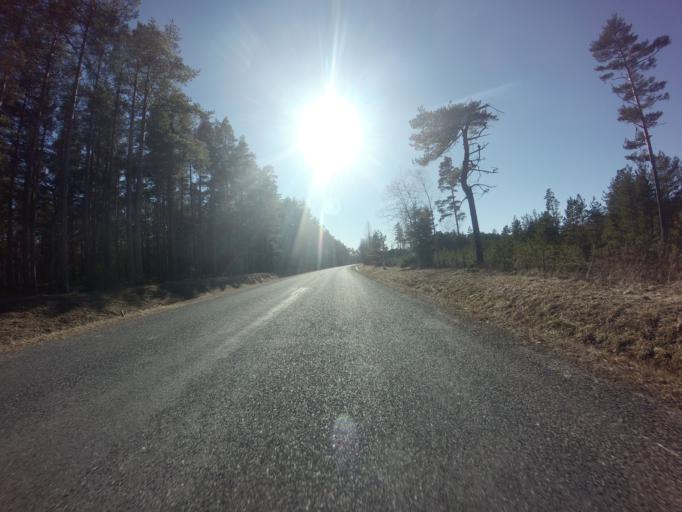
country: EE
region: Saare
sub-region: Kuressaare linn
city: Kuressaare
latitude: 58.5884
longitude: 22.5719
